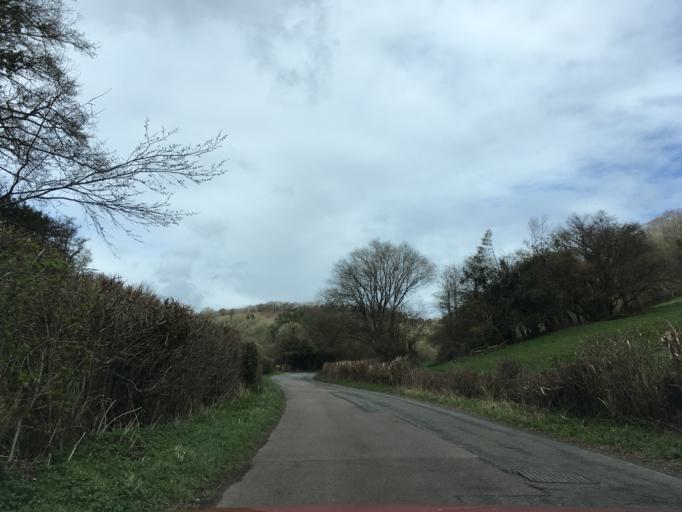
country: GB
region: England
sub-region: Gloucestershire
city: Coleford
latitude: 51.7816
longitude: -2.6319
